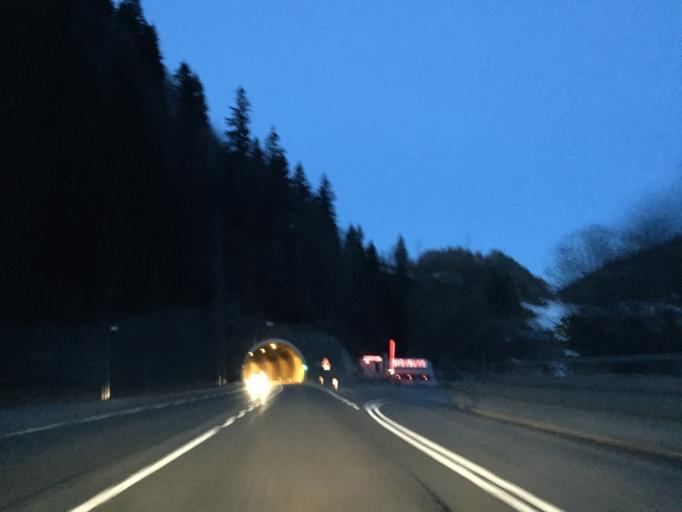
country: AT
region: Salzburg
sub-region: Politischer Bezirk Sankt Johann im Pongau
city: Goldegg
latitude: 47.3031
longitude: 13.1071
